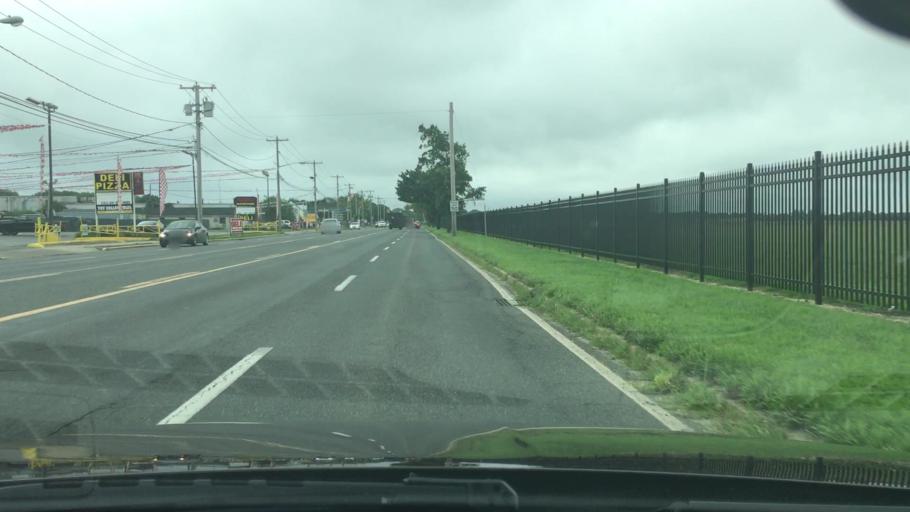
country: US
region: New York
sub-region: Suffolk County
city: East Farmingdale
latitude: 40.7306
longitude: -73.3978
